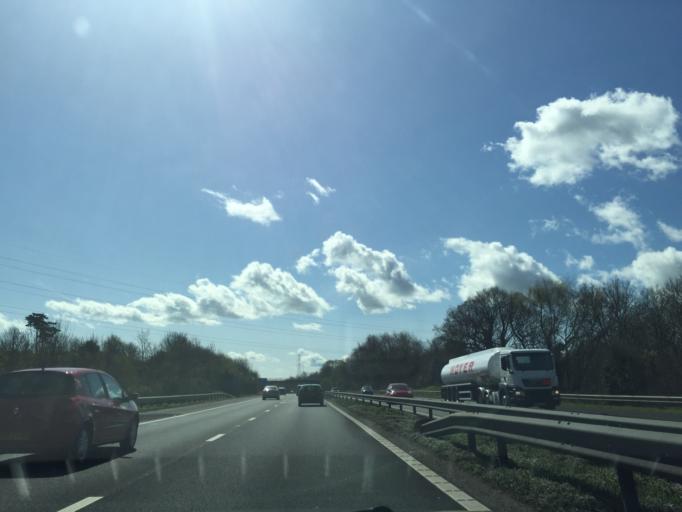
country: GB
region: England
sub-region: Hampshire
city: Waterlooville
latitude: 50.8676
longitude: -1.0163
